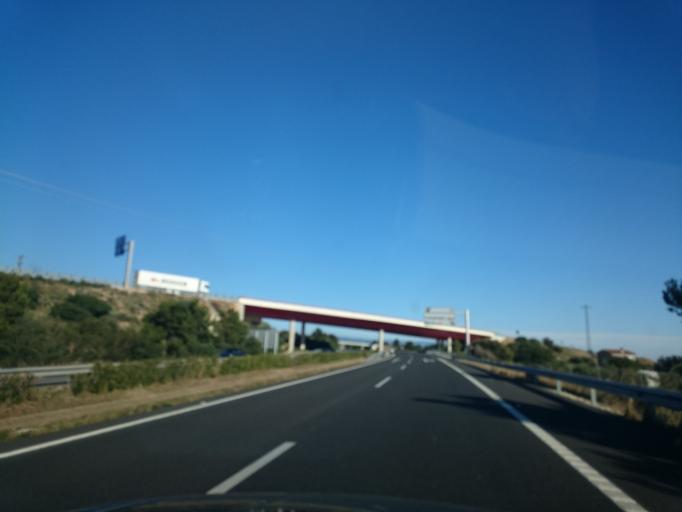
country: ES
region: Catalonia
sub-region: Provincia de Tarragona
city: Colldejou
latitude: 40.9970
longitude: 0.9082
